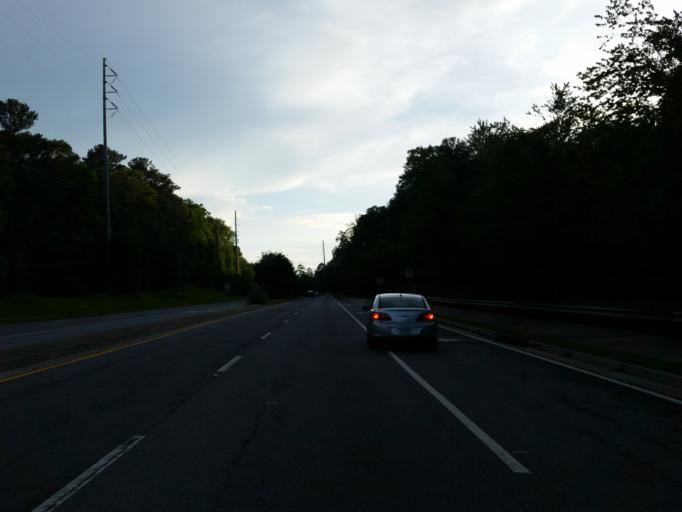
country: US
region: Georgia
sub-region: Fulton County
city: Roswell
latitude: 34.0100
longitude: -84.3807
